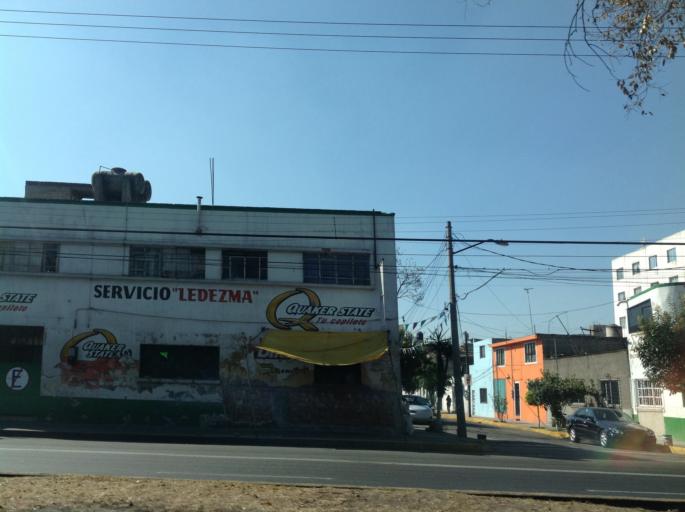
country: MX
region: Mexico City
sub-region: Iztacalco
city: Iztacalco
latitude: 19.4173
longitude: -99.0929
